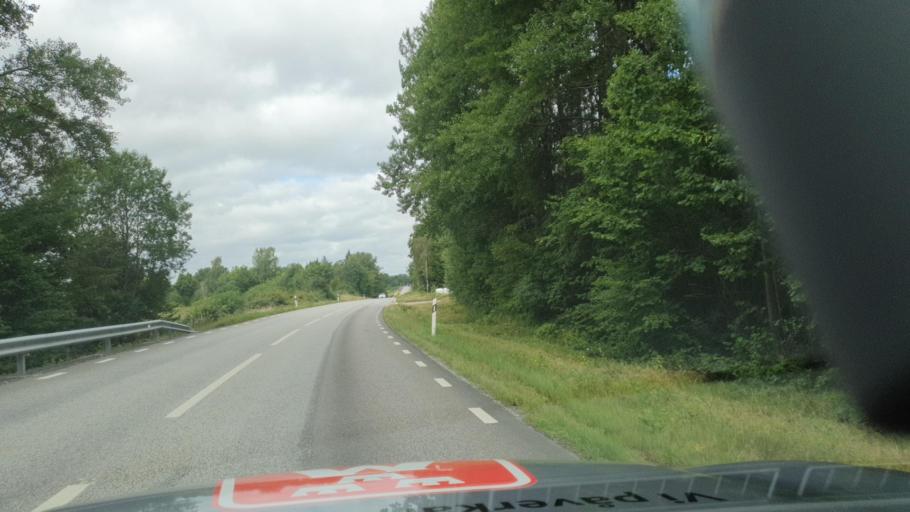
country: SE
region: Blekinge
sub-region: Karlskrona Kommun
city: Rodeby
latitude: 56.3003
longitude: 15.5820
